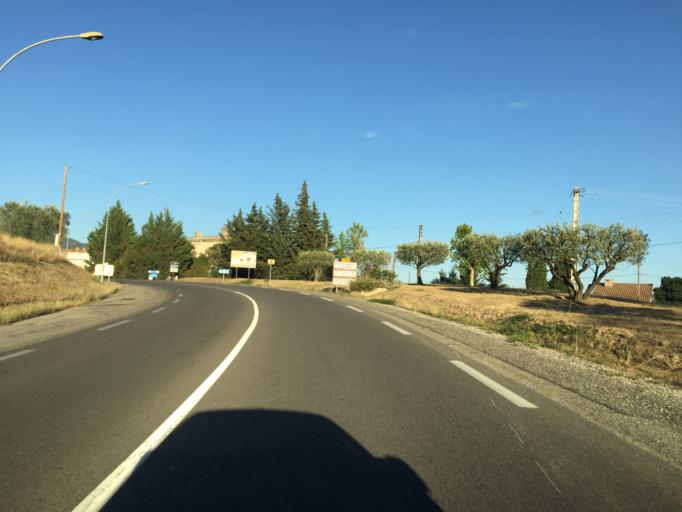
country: FR
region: Provence-Alpes-Cote d'Azur
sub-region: Departement des Alpes-de-Haute-Provence
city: Les Mees
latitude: 44.0674
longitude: 5.9813
